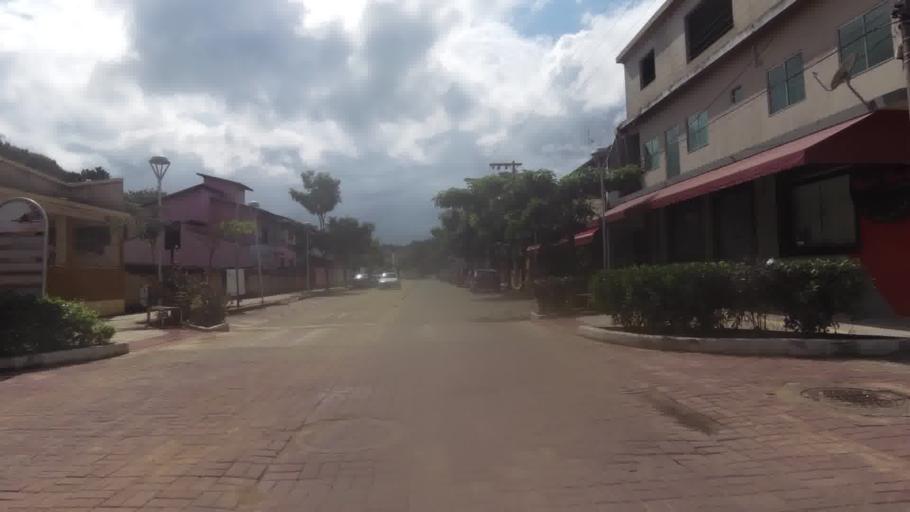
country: BR
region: Espirito Santo
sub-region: Piuma
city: Piuma
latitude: -20.8297
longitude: -40.6933
